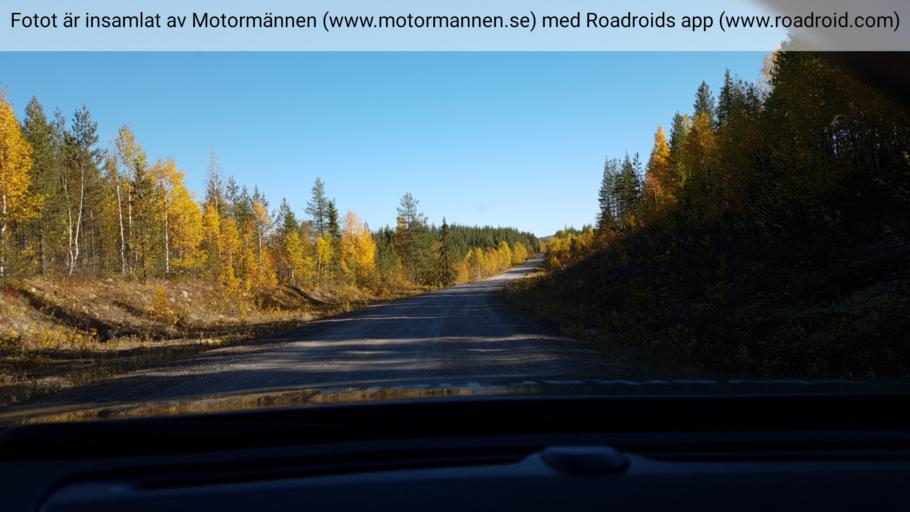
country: SE
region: Norrbotten
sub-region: Gallivare Kommun
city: Gaellivare
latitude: 66.5147
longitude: 20.9004
